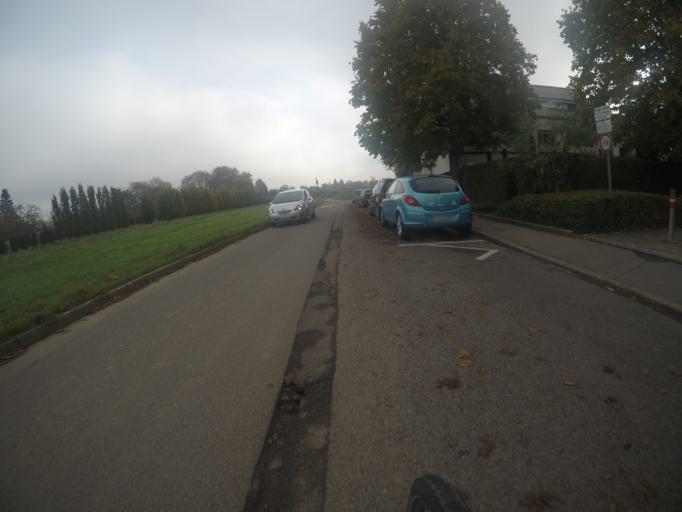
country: DE
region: Baden-Wuerttemberg
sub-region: Regierungsbezirk Stuttgart
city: Leinfelden-Echterdingen
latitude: 48.7338
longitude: 9.1396
